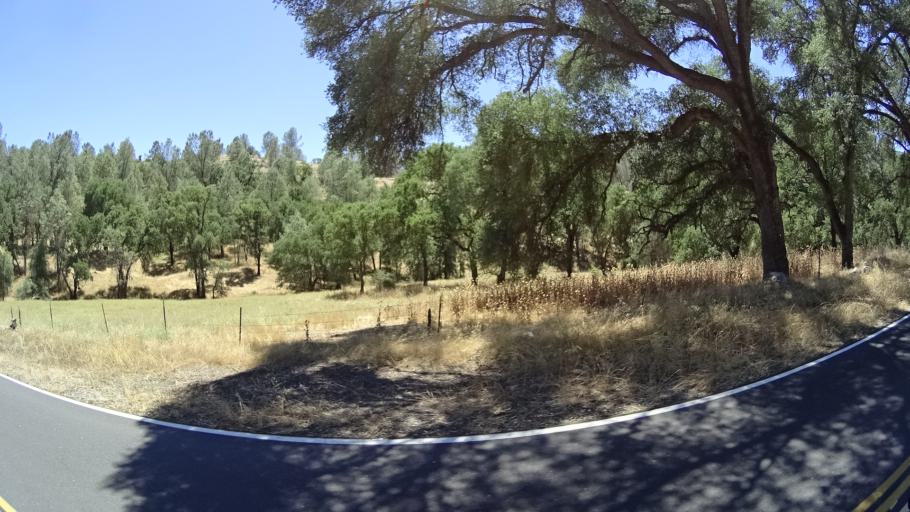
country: US
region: California
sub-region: Calaveras County
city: San Andreas
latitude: 38.1547
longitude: -120.6651
